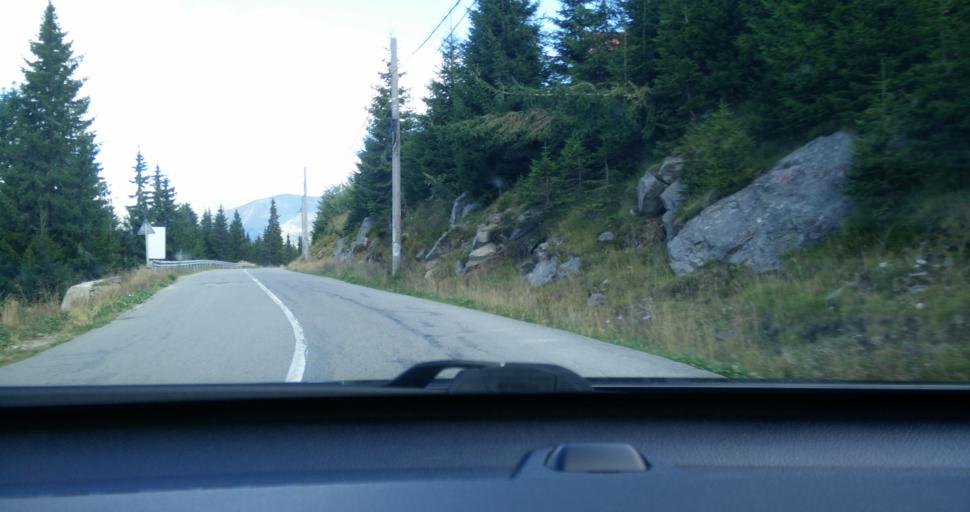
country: RO
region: Gorj
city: Novaci-Straini
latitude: 45.2876
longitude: 23.6922
